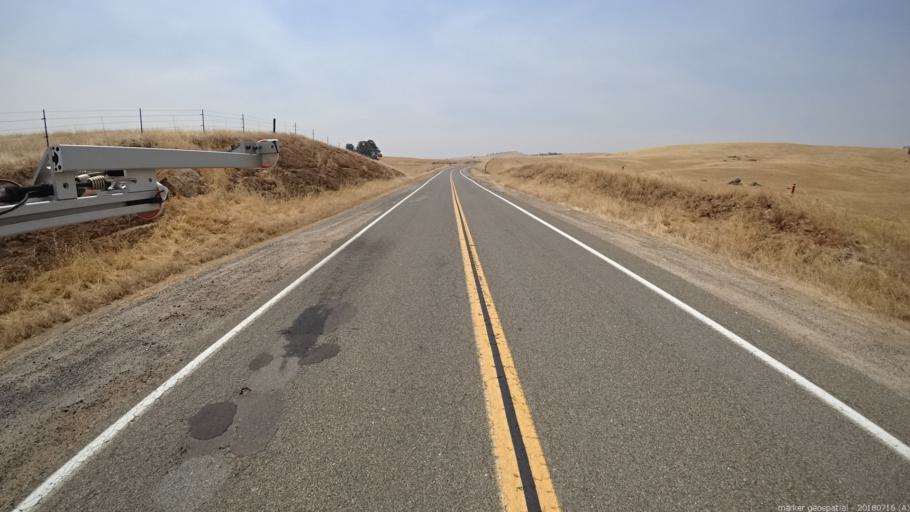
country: US
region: California
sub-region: Madera County
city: Bonadelle Ranchos-Madera Ranchos
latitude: 37.1331
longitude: -119.9180
